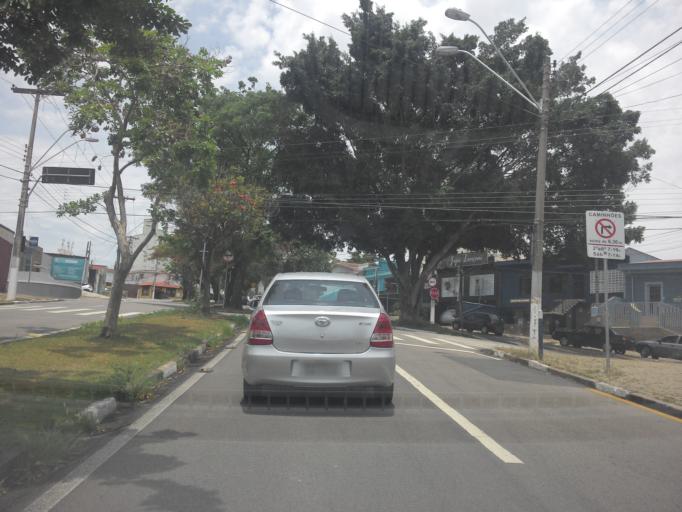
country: BR
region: Sao Paulo
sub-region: Campinas
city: Campinas
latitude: -22.9143
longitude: -47.0482
